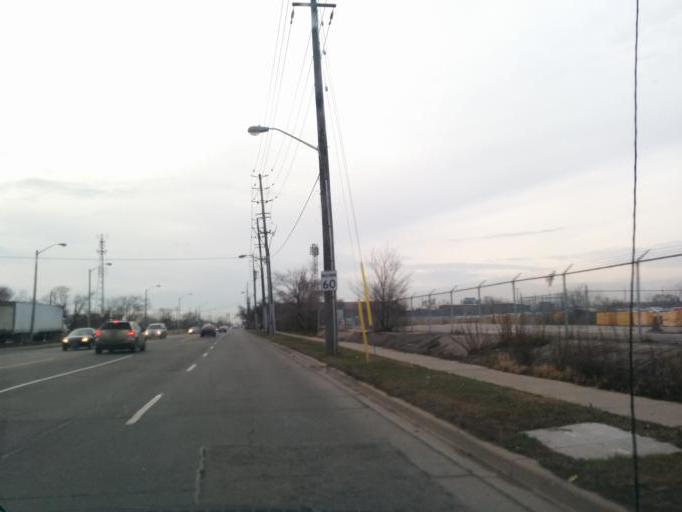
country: CA
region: Ontario
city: Etobicoke
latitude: 43.6238
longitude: -79.5353
